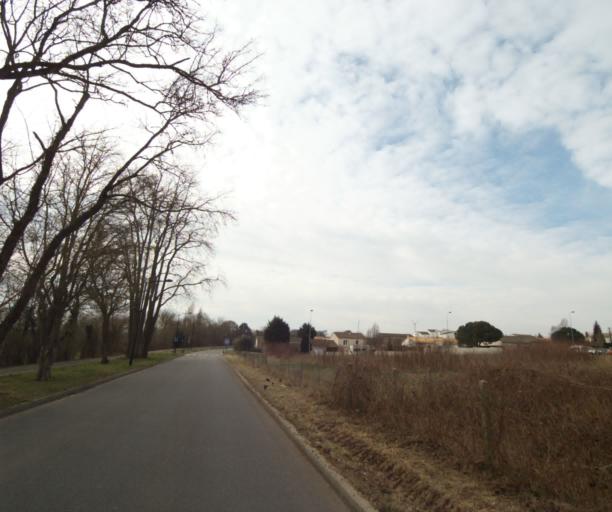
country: FR
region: Poitou-Charentes
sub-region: Departement des Deux-Sevres
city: Aiffres
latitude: 46.3150
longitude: -0.4292
